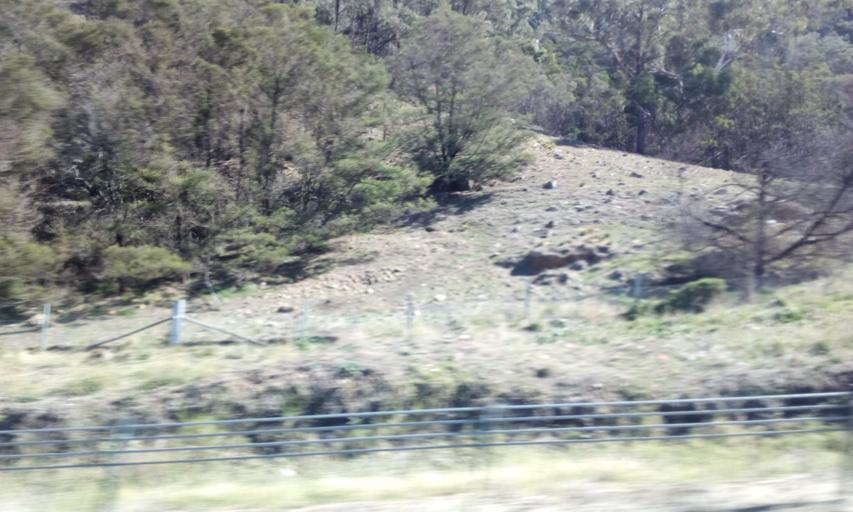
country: AU
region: New South Wales
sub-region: Yass Valley
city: Gundaroo
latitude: -35.0541
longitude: 149.3752
